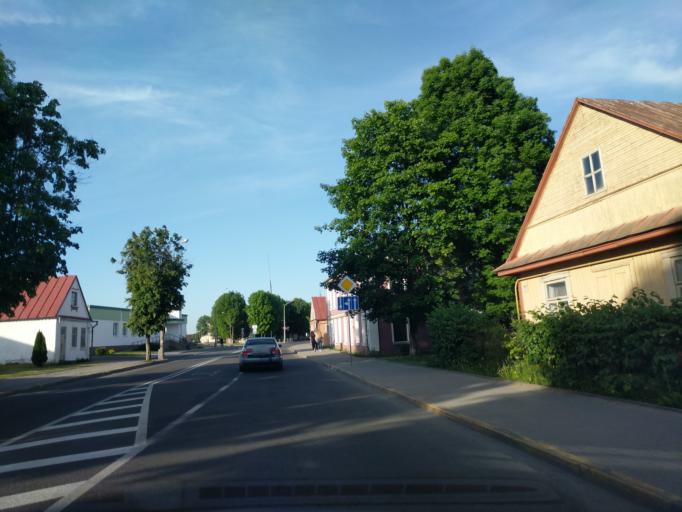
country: BY
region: Grodnenskaya
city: Ashmyany
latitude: 54.4275
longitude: 25.9418
